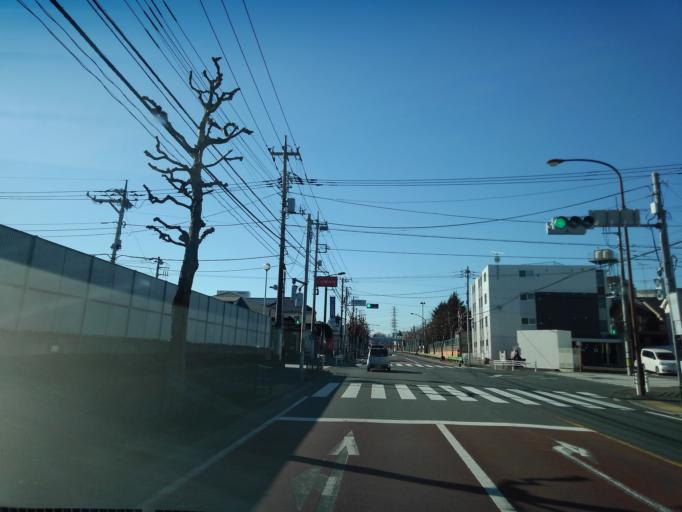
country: JP
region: Tokyo
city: Hino
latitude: 35.6722
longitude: 139.3618
